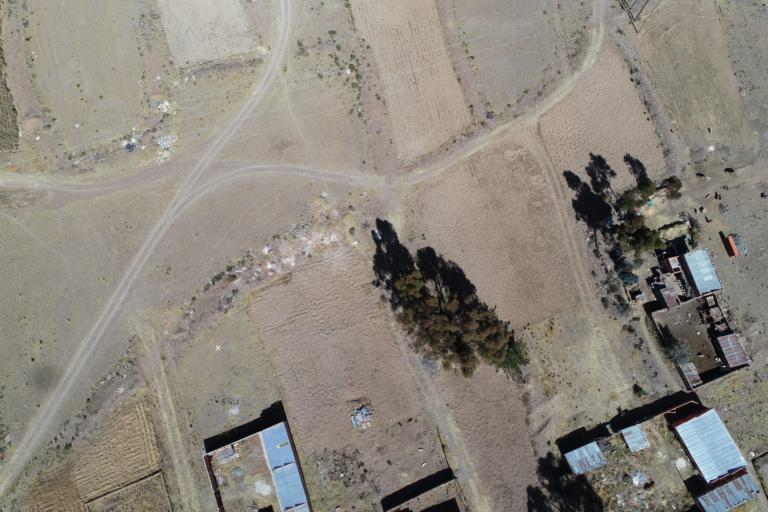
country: BO
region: La Paz
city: Achacachi
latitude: -15.8999
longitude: -68.9074
